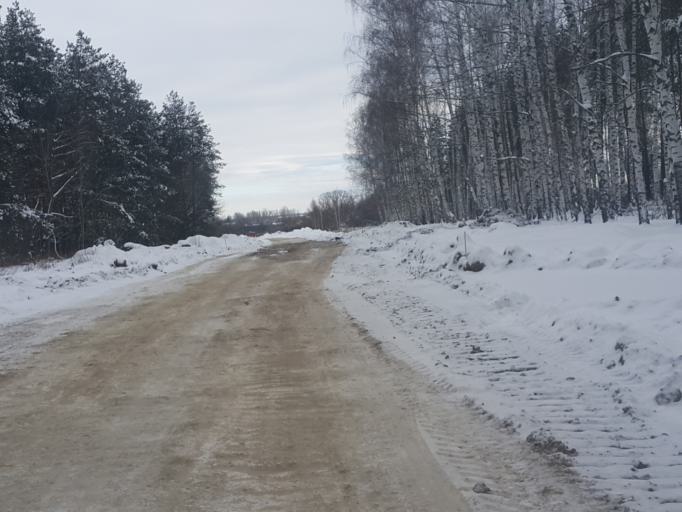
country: RU
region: Tambov
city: Platonovka
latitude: 52.8824
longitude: 41.8679
